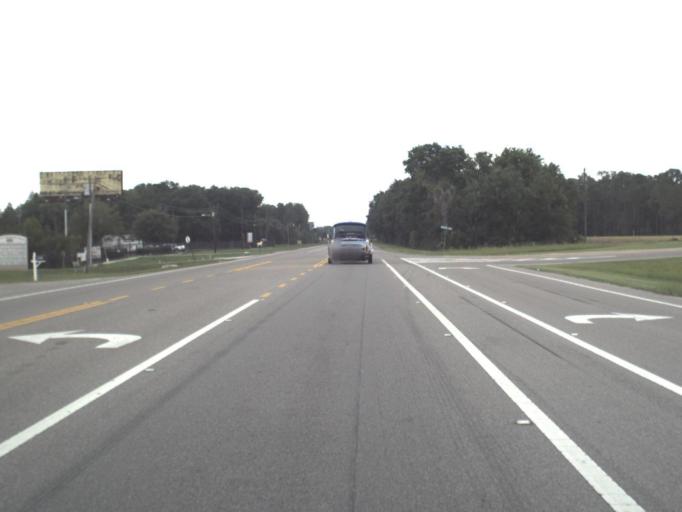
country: US
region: Florida
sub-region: Pasco County
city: Land O' Lakes
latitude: 28.2961
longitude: -82.4926
